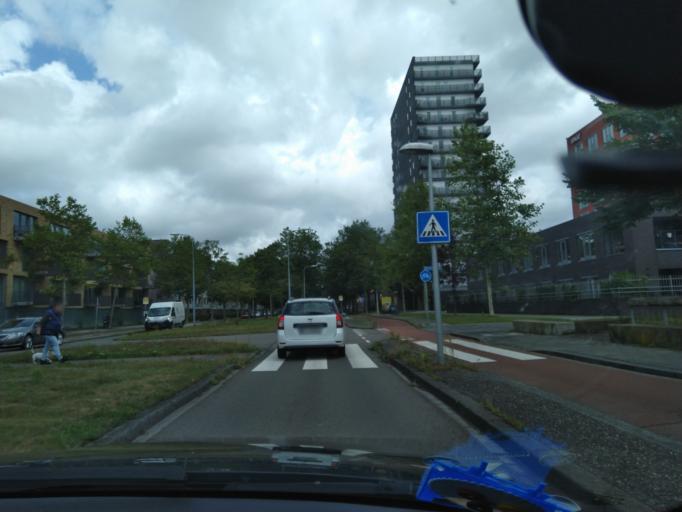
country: NL
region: Groningen
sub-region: Gemeente Groningen
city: Groningen
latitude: 53.2245
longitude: 6.5217
